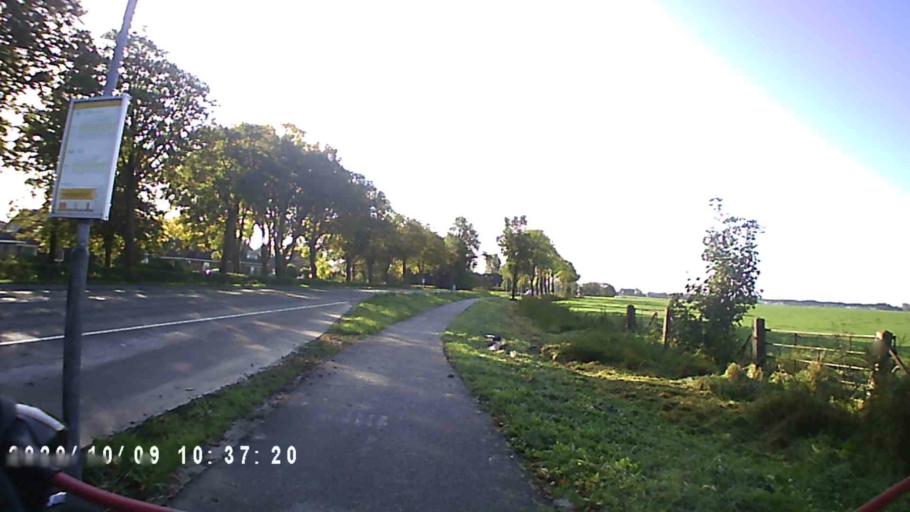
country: NL
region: Groningen
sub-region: Gemeente Winsum
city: Winsum
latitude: 53.2920
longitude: 6.5333
